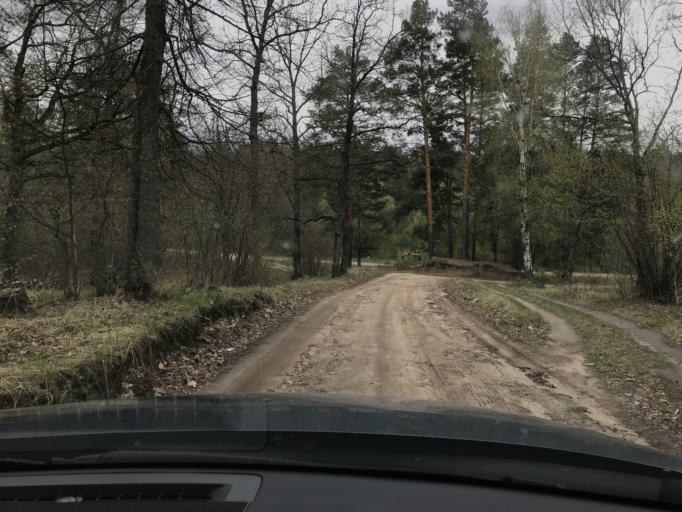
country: RU
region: Mordoviya
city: Shiringushi
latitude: 53.8552
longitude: 42.7864
